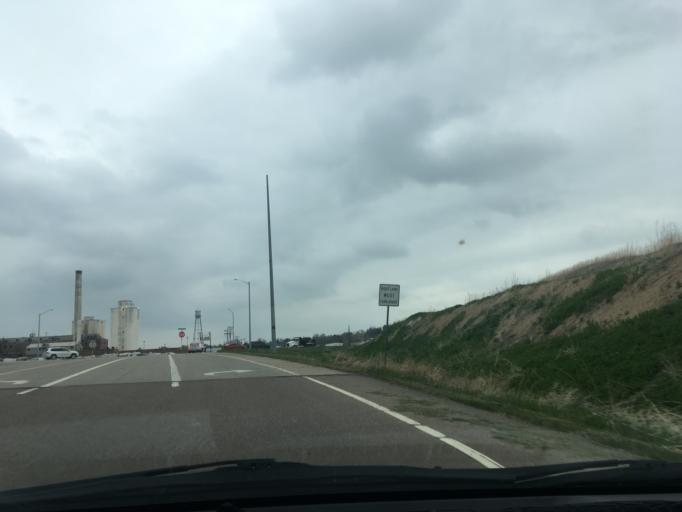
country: US
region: Colorado
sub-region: Boulder County
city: Longmont
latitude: 40.1545
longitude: -105.0742
